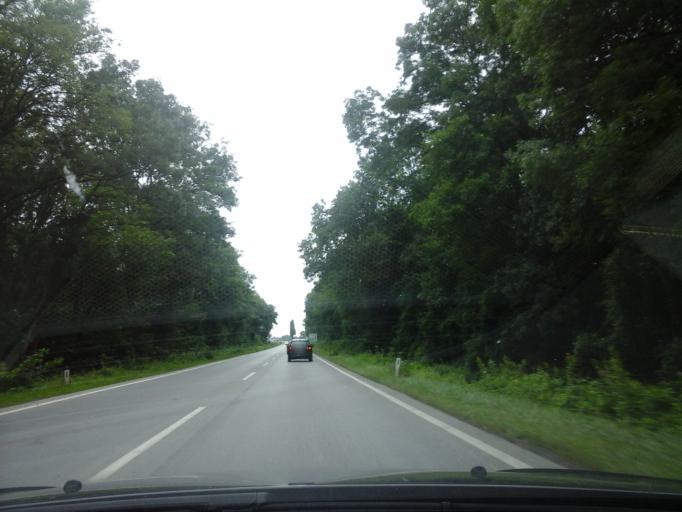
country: AT
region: Lower Austria
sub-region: Politischer Bezirk Ganserndorf
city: Engelhartstetten
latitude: 48.1596
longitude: 16.8990
